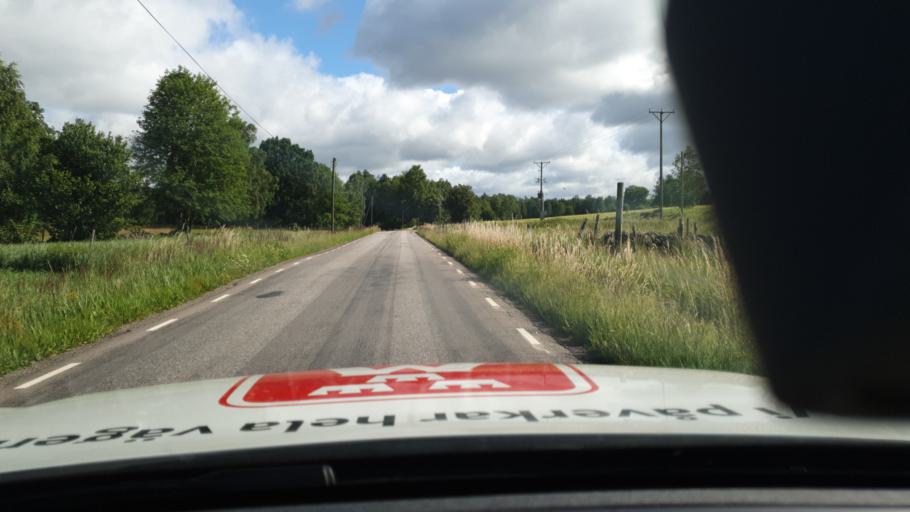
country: SE
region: Vaestra Goetaland
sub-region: Falkopings Kommun
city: Floby
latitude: 58.1648
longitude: 13.3402
